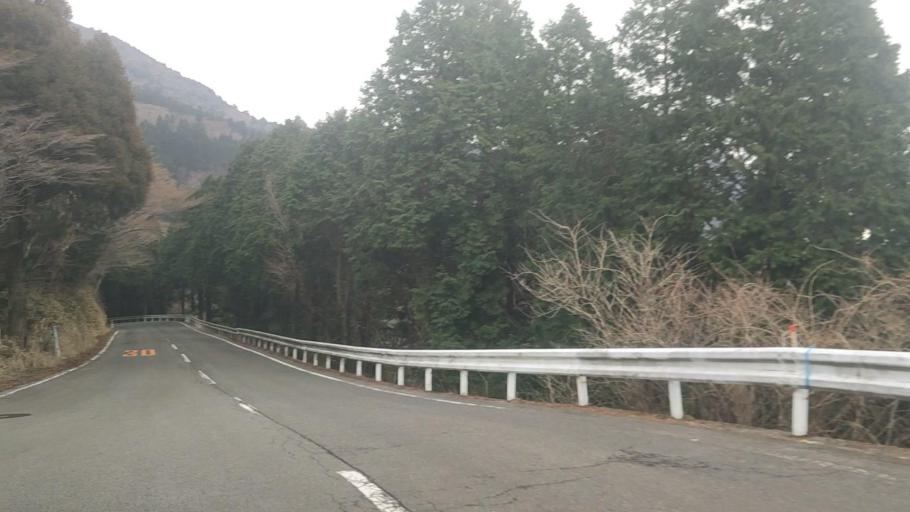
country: JP
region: Nagasaki
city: Shimabara
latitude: 32.7553
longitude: 130.2744
